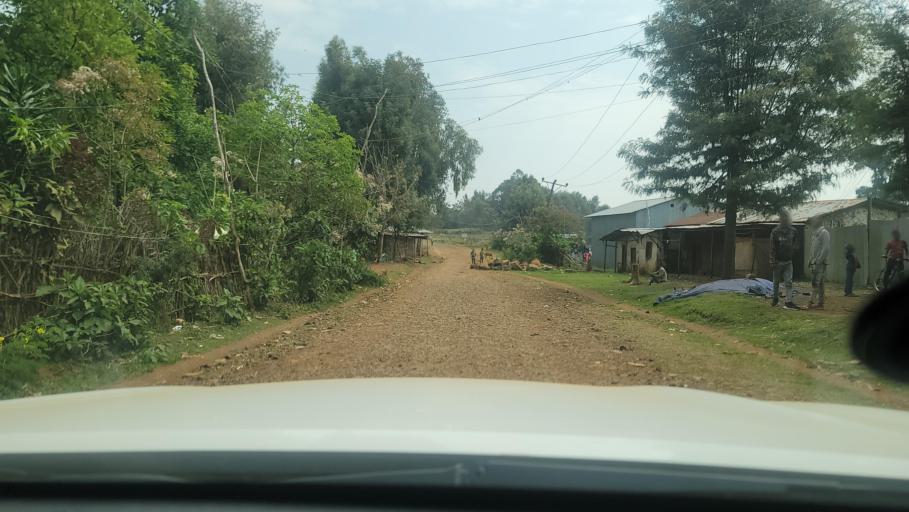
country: ET
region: Oromiya
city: Agaro
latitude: 7.8106
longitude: 36.4721
